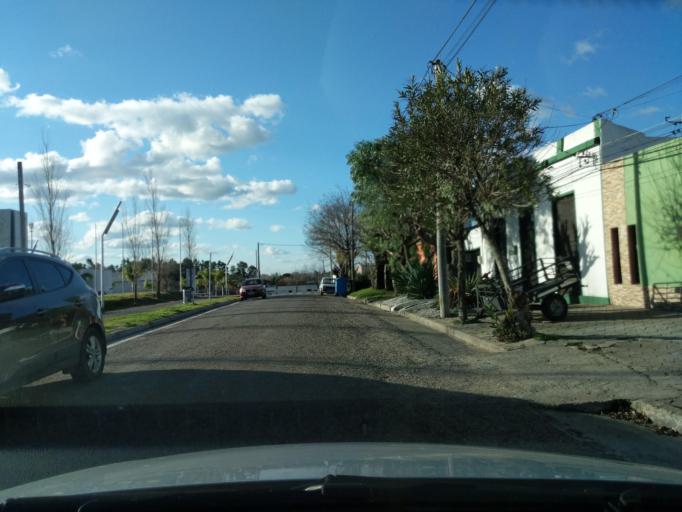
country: UY
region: Florida
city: Florida
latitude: -34.0994
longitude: -56.2315
